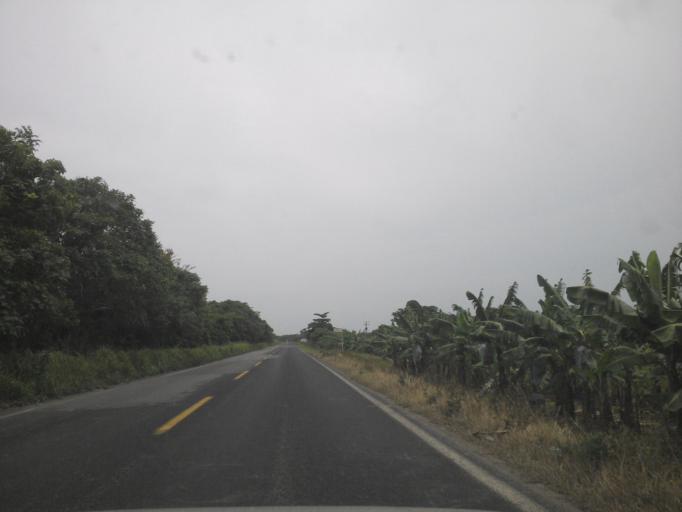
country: MX
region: Veracruz
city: Nautla
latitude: 20.2173
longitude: -96.8149
